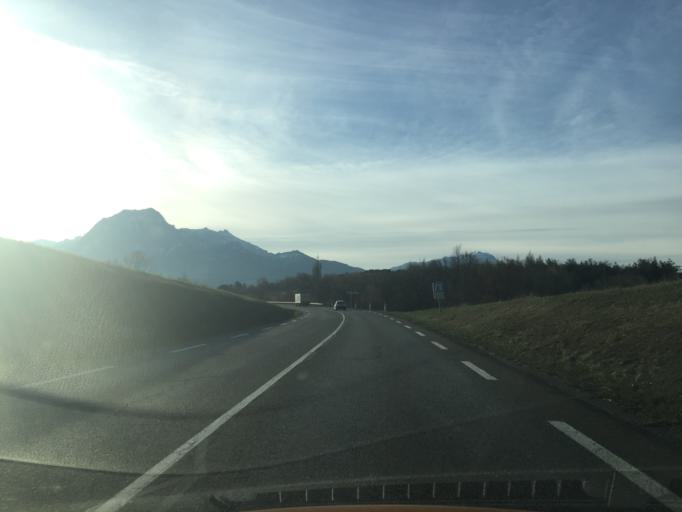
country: FR
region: Provence-Alpes-Cote d'Azur
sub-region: Departement des Hautes-Alpes
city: Chorges
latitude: 44.5363
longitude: 6.2990
